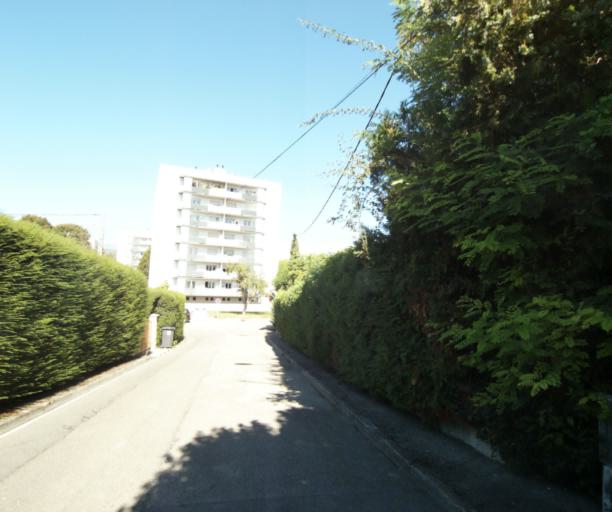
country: FR
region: Rhone-Alpes
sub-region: Departement de l'Ain
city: Ferney-Voltaire
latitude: 46.2565
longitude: 6.1204
